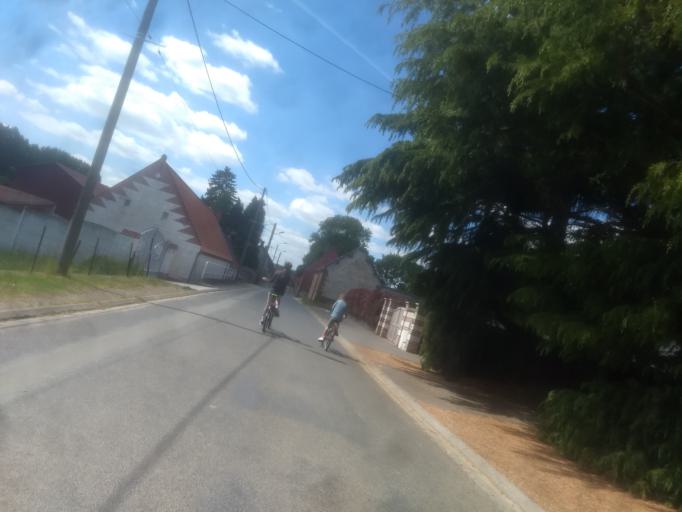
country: FR
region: Nord-Pas-de-Calais
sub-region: Departement du Pas-de-Calais
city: Riviere
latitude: 50.2368
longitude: 2.6929
